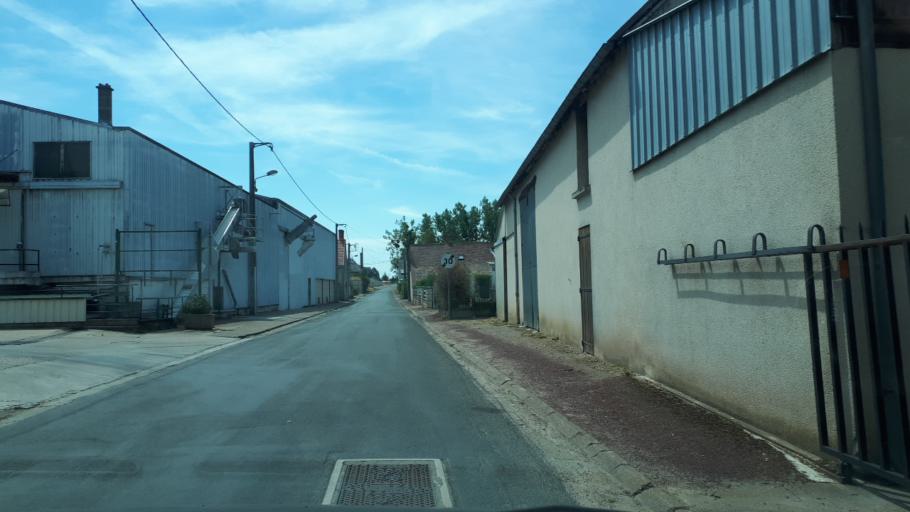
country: FR
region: Centre
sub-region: Departement du Loir-et-Cher
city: Contres
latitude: 47.3894
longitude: 1.3778
